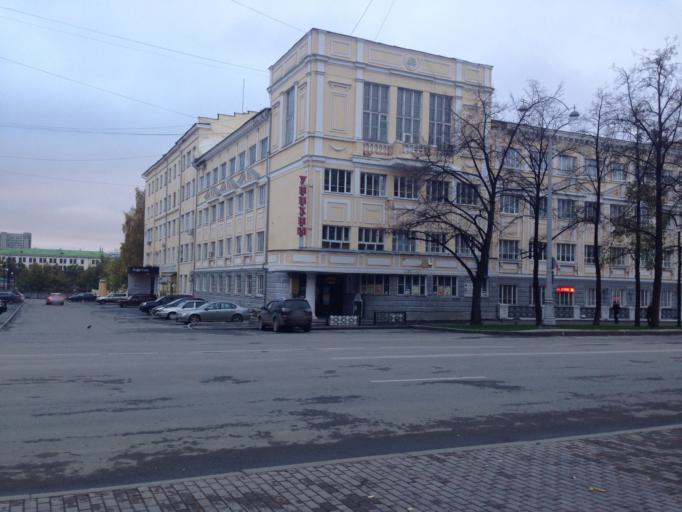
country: RU
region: Sverdlovsk
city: Yekaterinburg
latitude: 56.8399
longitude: 60.5979
